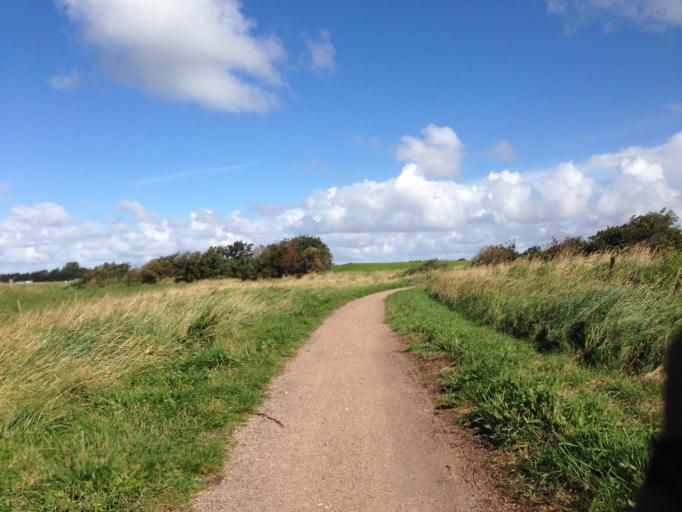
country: DE
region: Schleswig-Holstein
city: Borgsum
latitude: 54.6932
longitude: 8.4573
